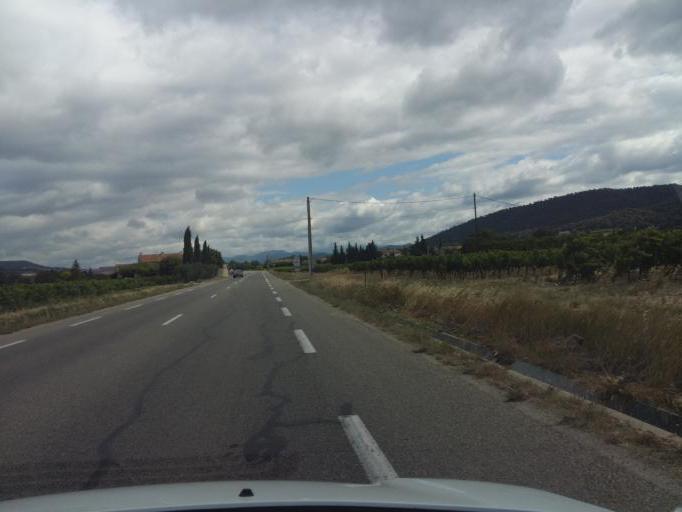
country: FR
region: Provence-Alpes-Cote d'Azur
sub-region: Departement du Vaucluse
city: Sablet
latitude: 44.2152
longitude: 5.0057
